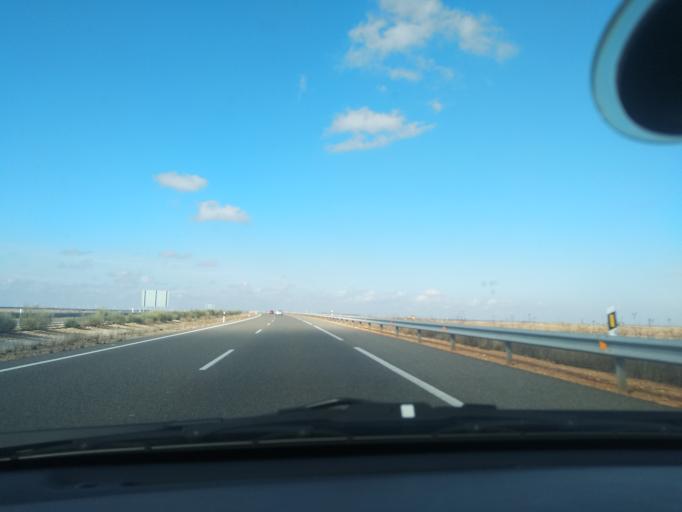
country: ES
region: Castille and Leon
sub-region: Provincia de Valladolid
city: Villanubla
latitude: 41.7246
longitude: -4.8309
